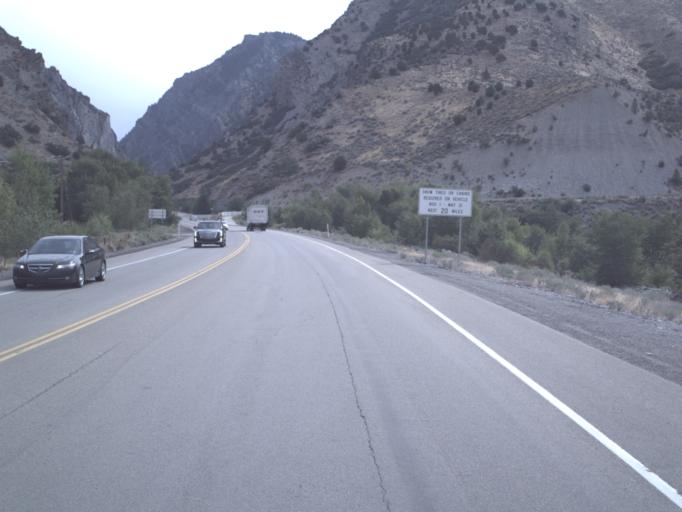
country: US
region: Utah
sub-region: Utah County
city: Cedar Hills
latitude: 40.4317
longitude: -111.7557
